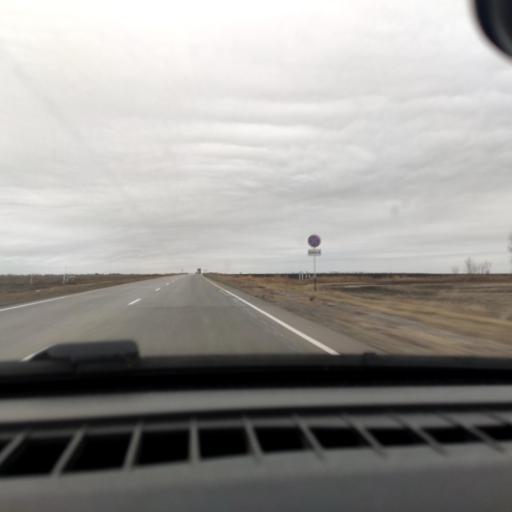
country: RU
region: Voronezj
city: Strelitsa
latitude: 51.4750
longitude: 38.9606
